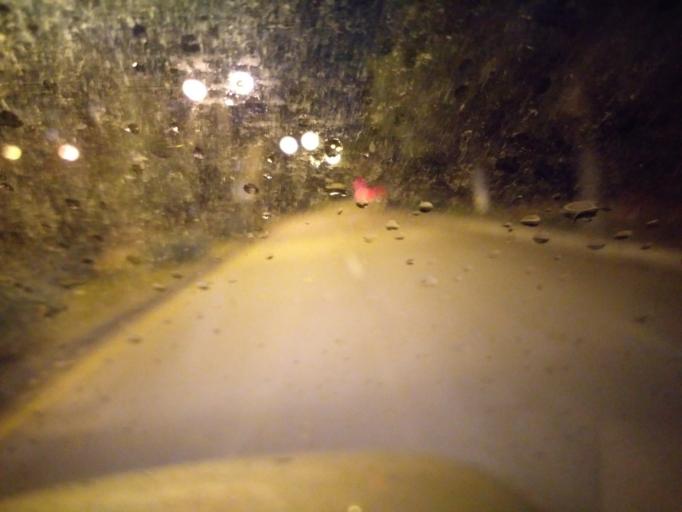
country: TR
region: Ankara
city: Batikent
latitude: 39.8790
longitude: 32.7134
